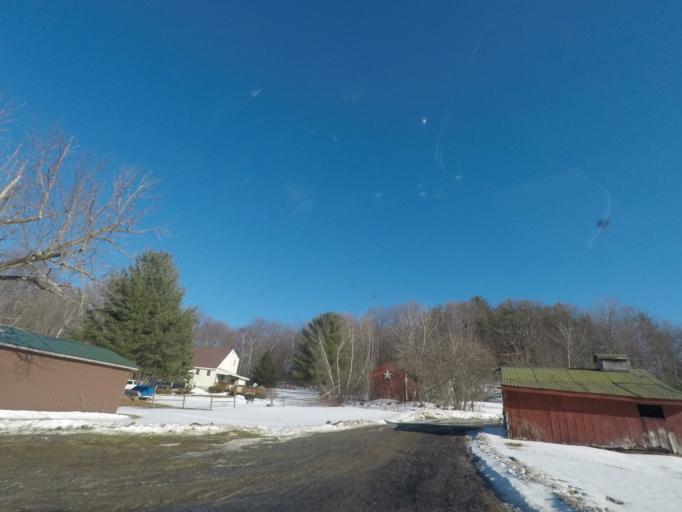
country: US
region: New York
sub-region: Rensselaer County
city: Averill Park
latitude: 42.6412
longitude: -73.5029
